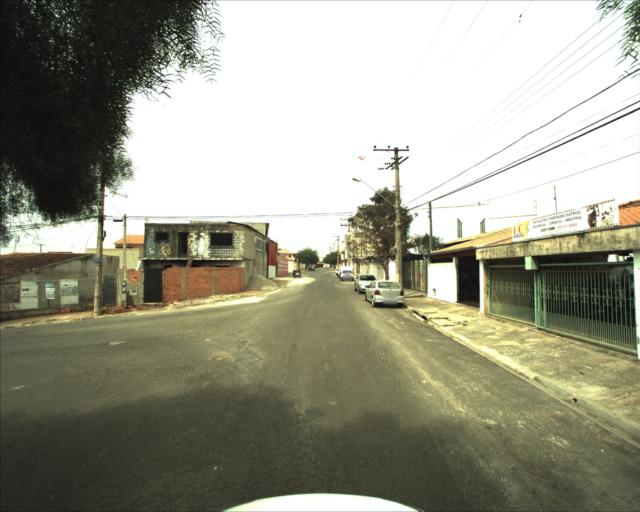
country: BR
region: Sao Paulo
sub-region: Sorocaba
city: Sorocaba
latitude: -23.4960
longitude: -47.5291
